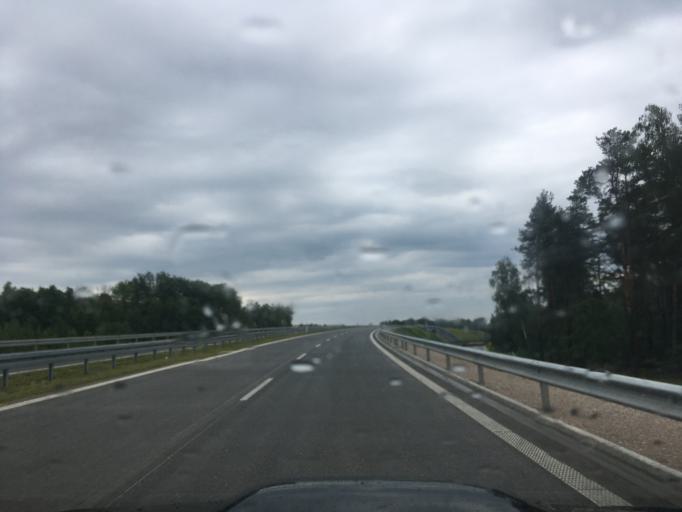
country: PL
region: Masovian Voivodeship
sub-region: Powiat piaseczynski
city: Gora Kalwaria
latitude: 51.9834
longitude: 21.1747
